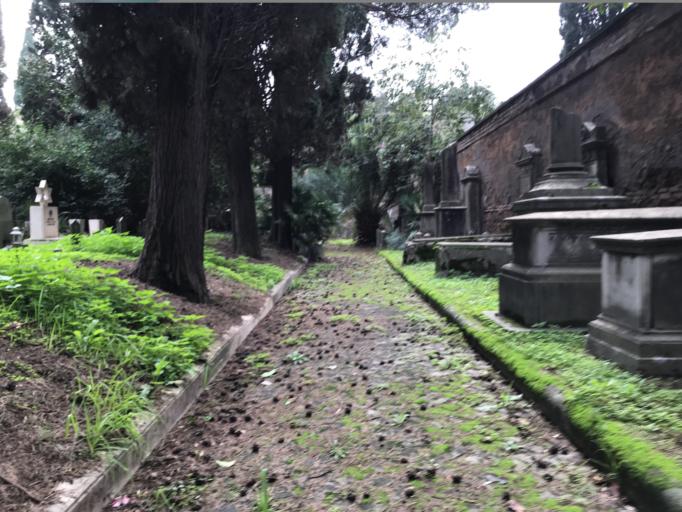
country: IT
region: Latium
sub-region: Citta metropolitana di Roma Capitale
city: Rome
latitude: 41.9073
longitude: 12.5280
